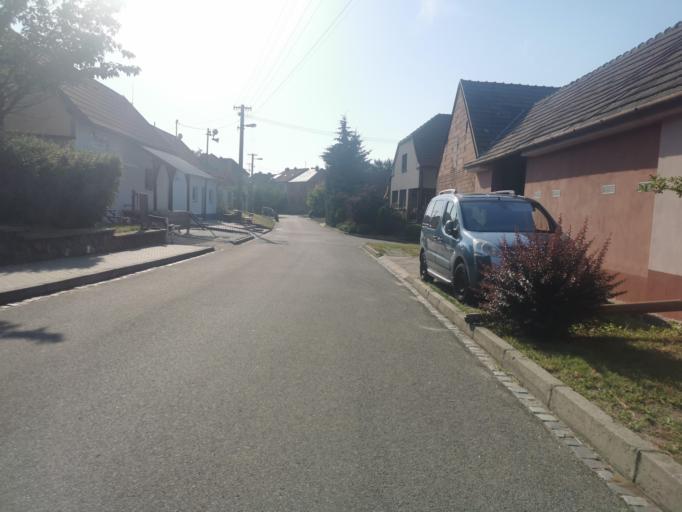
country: CZ
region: South Moravian
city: Vacenovice
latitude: 48.9437
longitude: 17.1731
